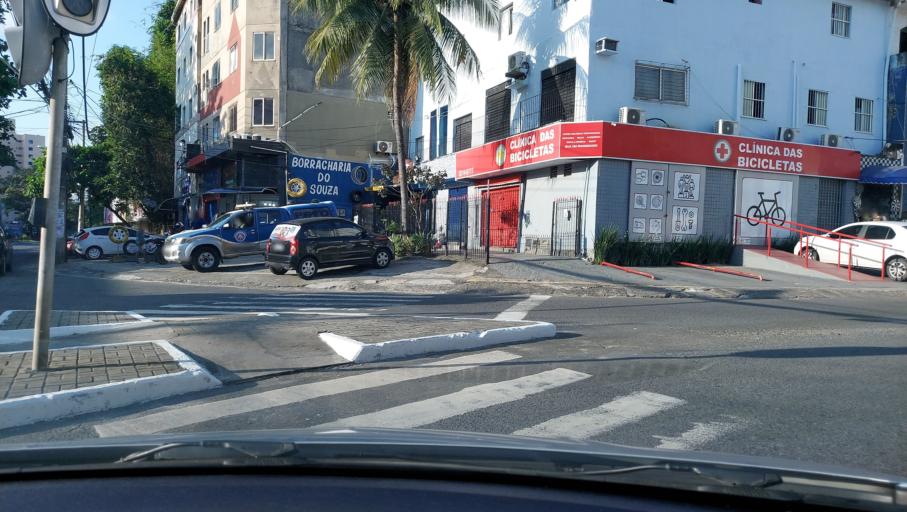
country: BR
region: Bahia
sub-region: Salvador
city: Salvador
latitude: -12.9888
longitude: -38.4480
